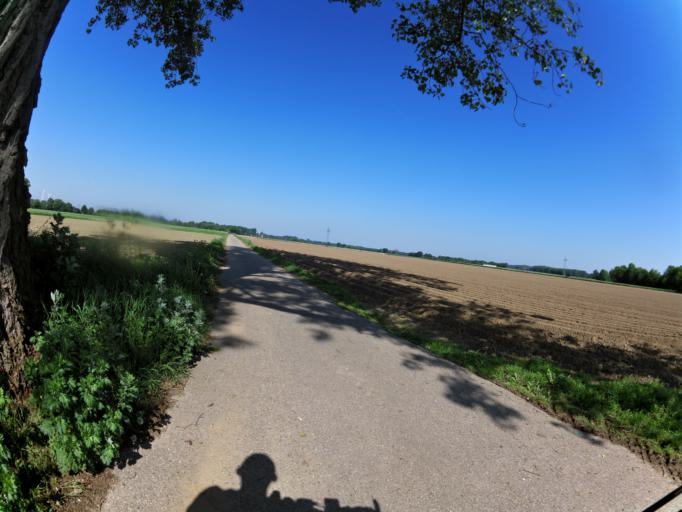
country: DE
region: North Rhine-Westphalia
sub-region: Regierungsbezirk Koln
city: Linnich
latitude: 50.9993
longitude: 6.2703
